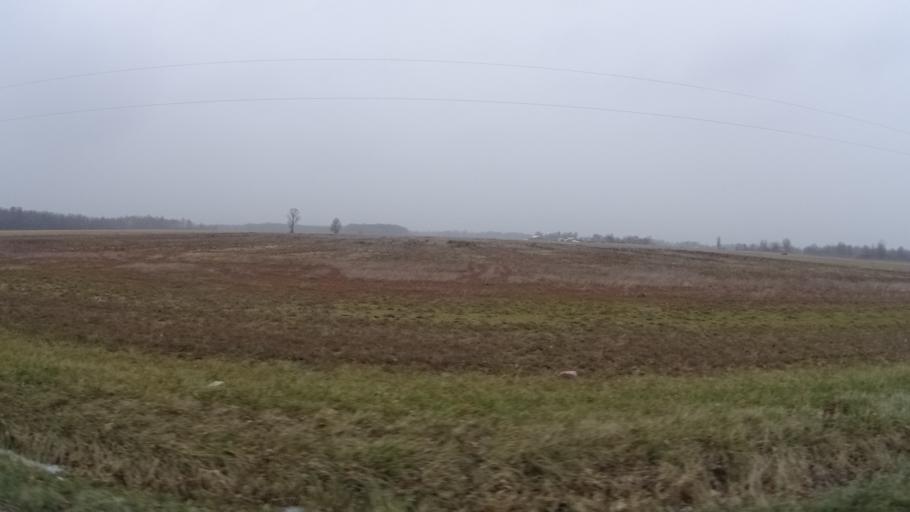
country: US
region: Ohio
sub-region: Lorain County
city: Oberlin
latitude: 41.3377
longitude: -82.1998
